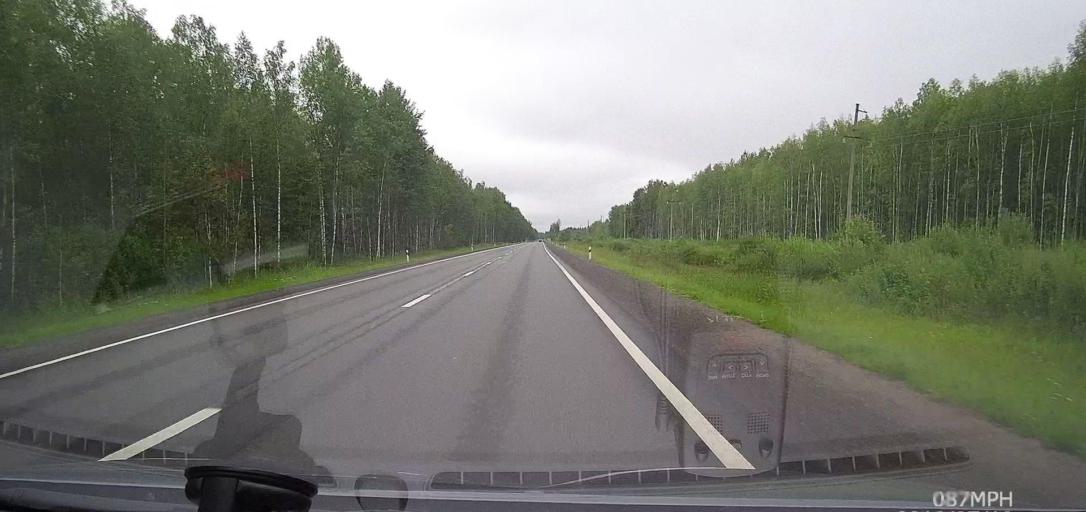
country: RU
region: Leningrad
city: Syas'stroy
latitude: 60.2247
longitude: 32.7188
